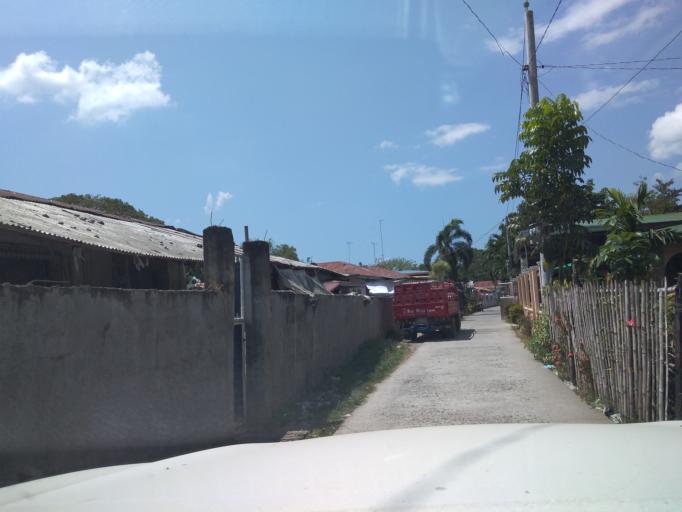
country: PH
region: Central Luzon
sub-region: Province of Pampanga
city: Lourdes
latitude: 15.0090
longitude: 120.8678
